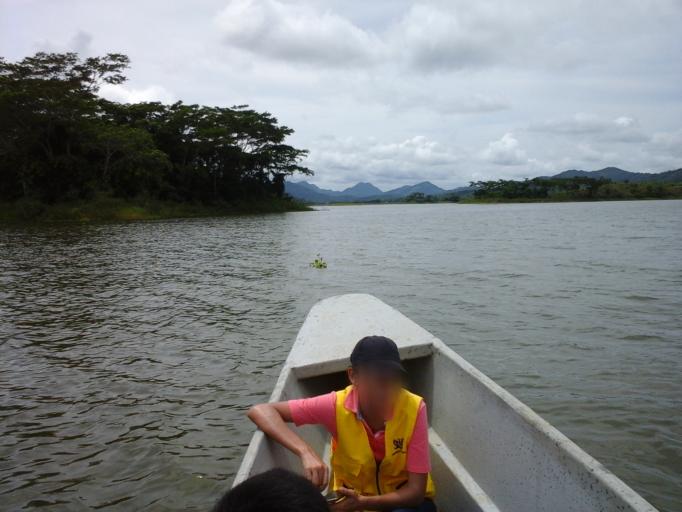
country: CO
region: Bolivar
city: San Cristobal
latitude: 9.8742
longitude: -75.3010
